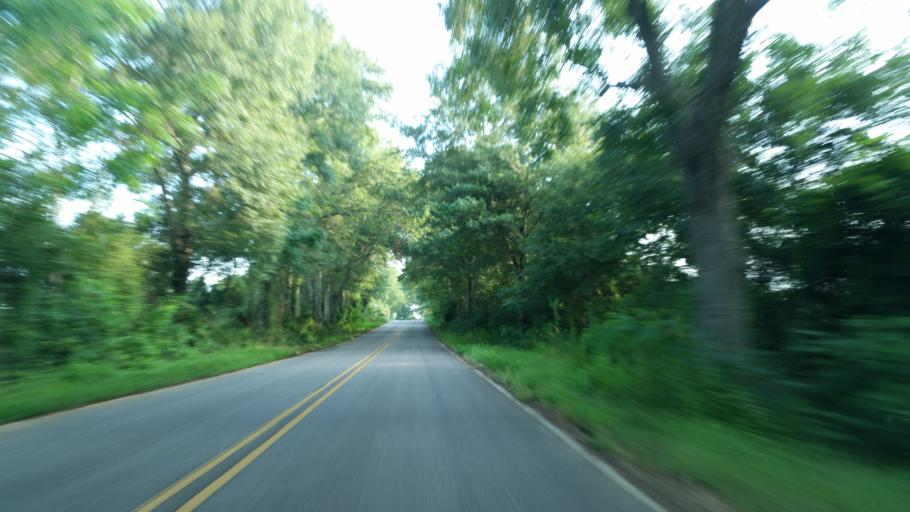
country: US
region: Alabama
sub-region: Escambia County
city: Atmore
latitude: 30.9948
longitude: -87.5711
